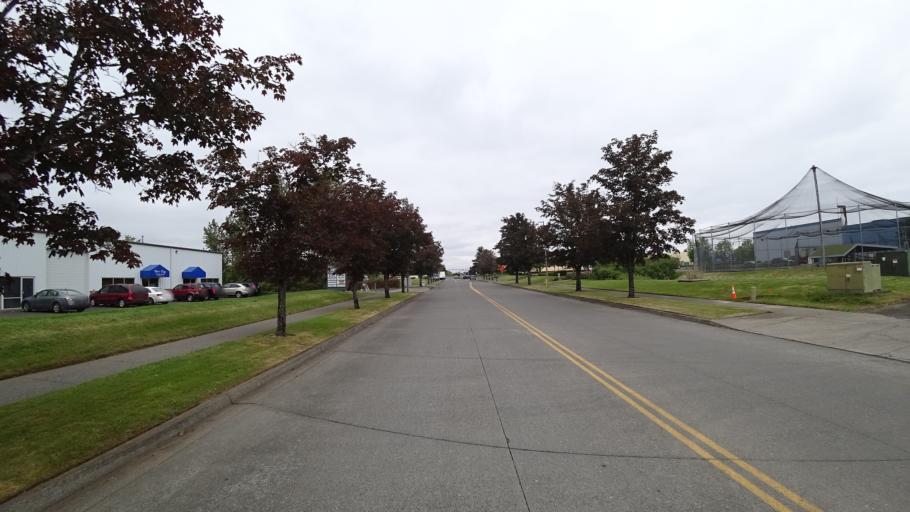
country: US
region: Oregon
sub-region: Washington County
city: Aloha
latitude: 45.4957
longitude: -122.9182
